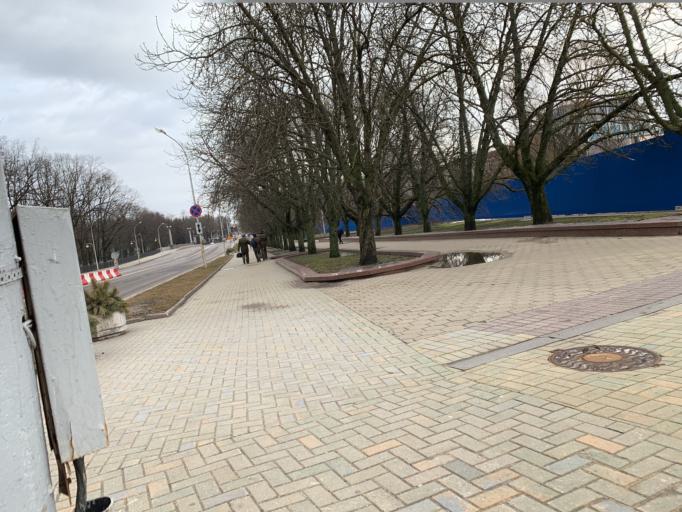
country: BY
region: Minsk
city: Minsk
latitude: 53.9079
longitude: 27.5613
